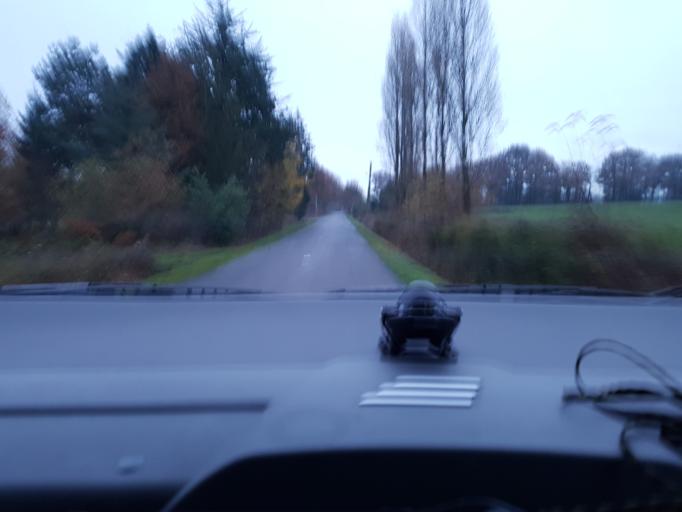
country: FR
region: Brittany
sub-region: Departement d'Ille-et-Vilaine
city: Livre-sur-Changeon
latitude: 48.2497
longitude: -1.3425
